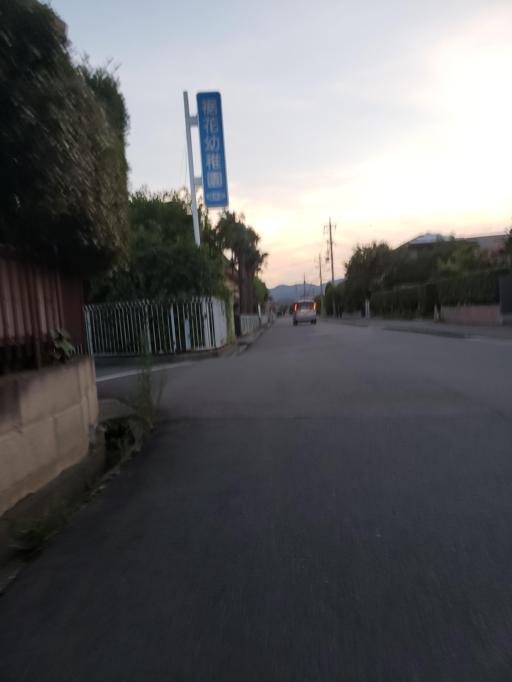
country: JP
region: Nagano
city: Nagano-shi
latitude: 36.6314
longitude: 138.1691
